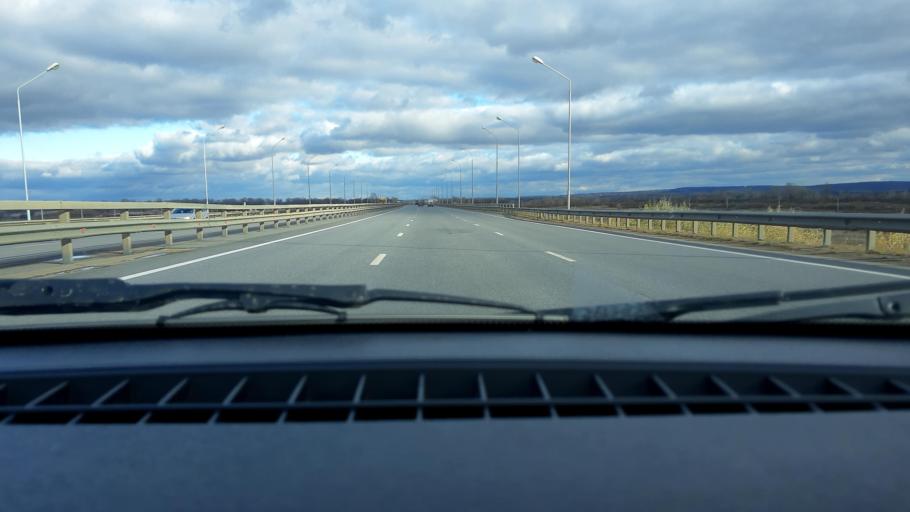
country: RU
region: Bashkortostan
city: Ufa
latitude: 54.6424
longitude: 55.9523
